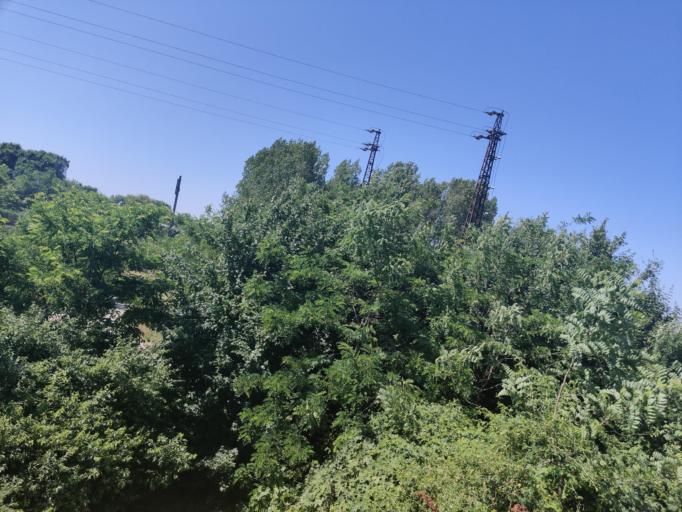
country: HU
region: Hajdu-Bihar
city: Balmazujvaros
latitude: 47.6043
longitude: 21.3789
